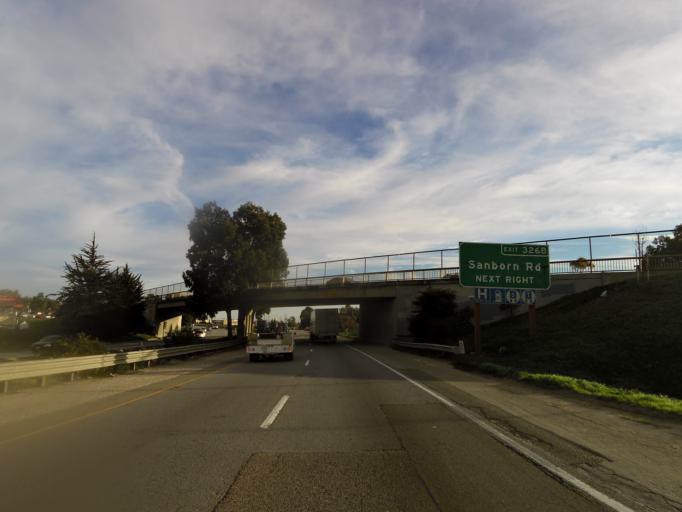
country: US
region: California
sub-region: Monterey County
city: Salinas
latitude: 36.6715
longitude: -121.6398
